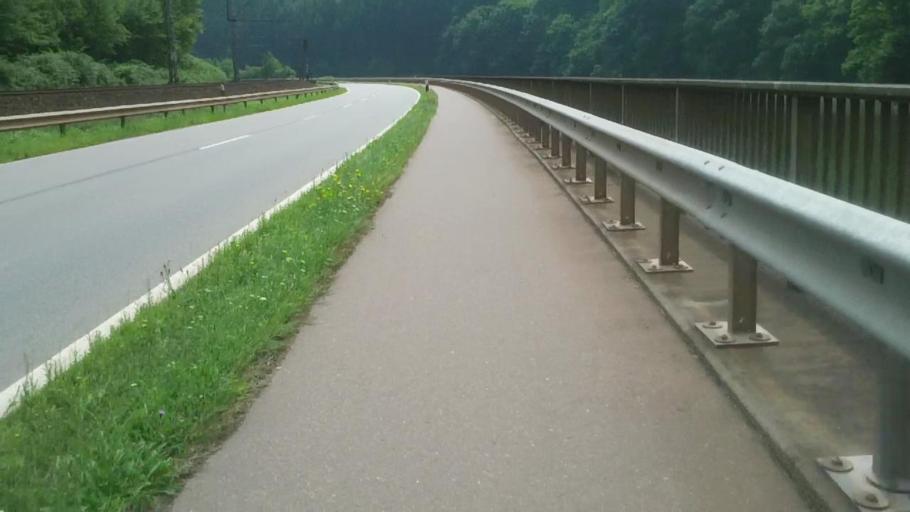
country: DE
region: Rheinland-Pfalz
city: Taben-Rodt
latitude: 49.5565
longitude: 6.5973
